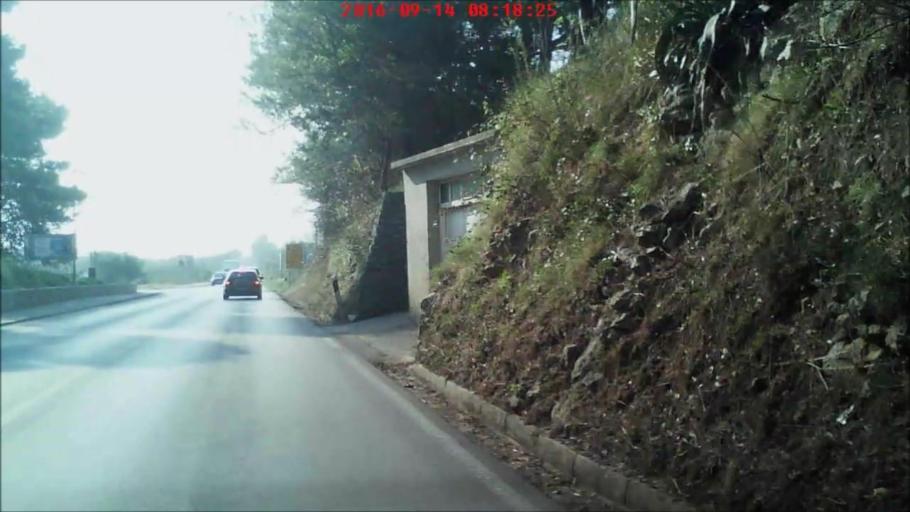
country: HR
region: Zadarska
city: Nin
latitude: 44.2383
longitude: 15.1844
